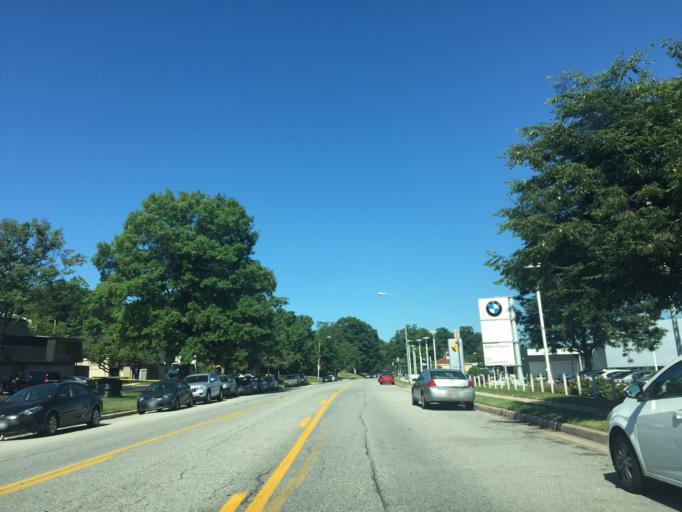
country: US
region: Maryland
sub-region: Baltimore County
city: Lutherville
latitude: 39.4100
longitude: -76.6167
